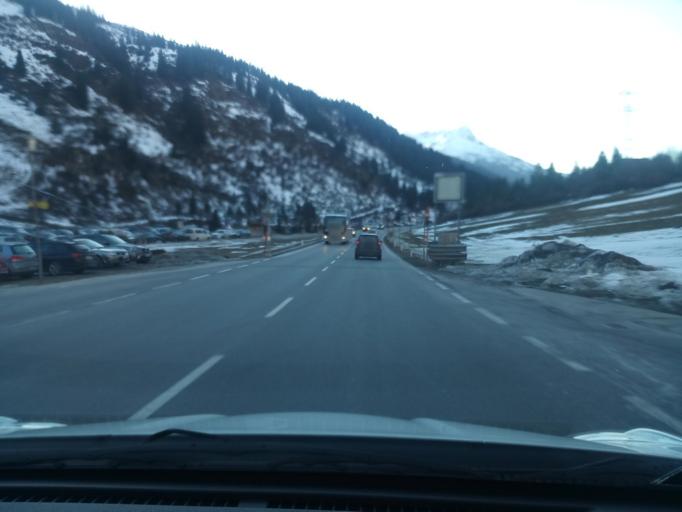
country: AT
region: Vorarlberg
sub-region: Politischer Bezirk Bludenz
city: Lech
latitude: 47.1396
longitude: 10.1579
